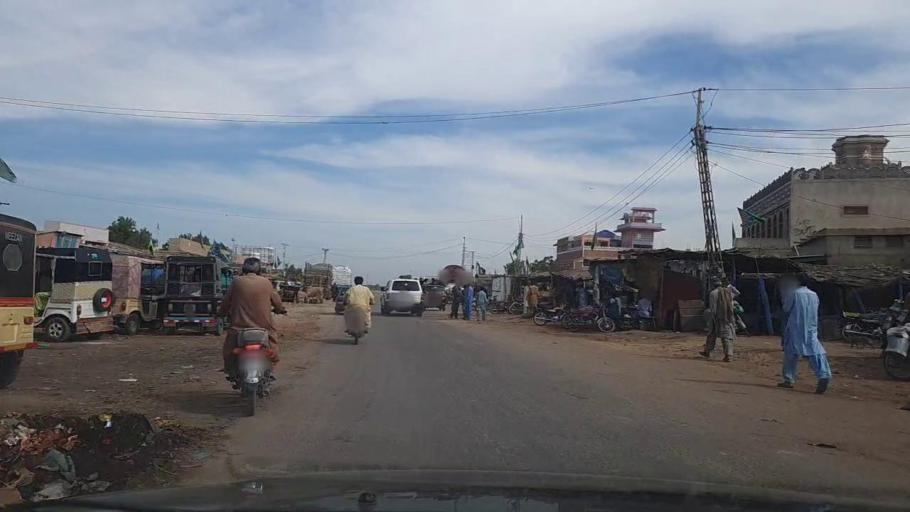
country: PK
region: Sindh
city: Thatta
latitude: 24.7935
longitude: 67.9584
